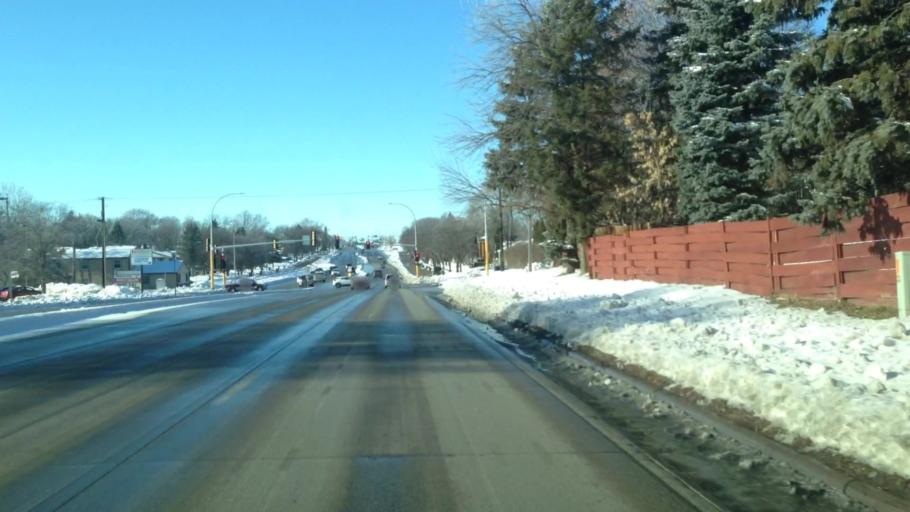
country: US
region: Minnesota
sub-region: Olmsted County
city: Rochester
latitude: 44.0617
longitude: -92.4872
